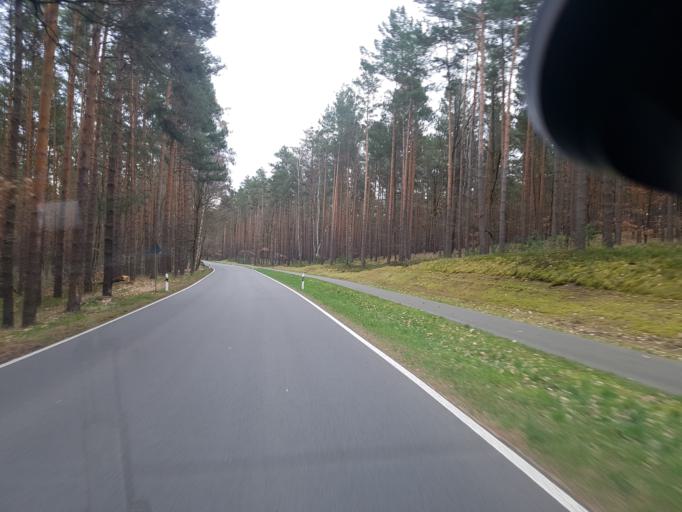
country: DE
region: Brandenburg
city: Gross Lindow
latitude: 52.1604
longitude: 14.5043
